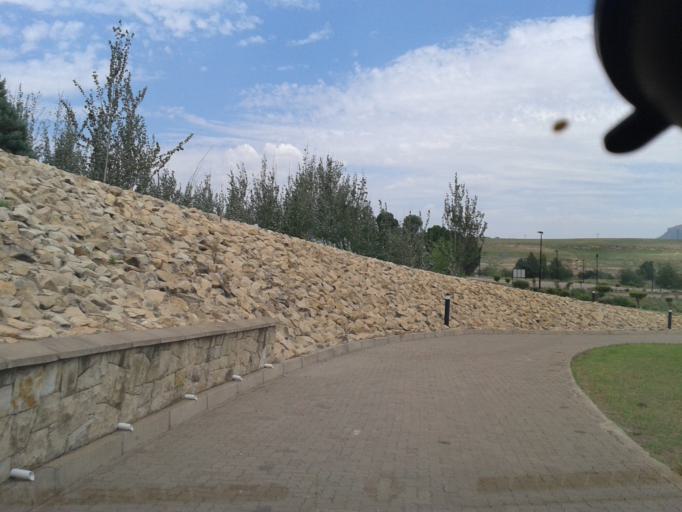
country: LS
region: Maseru
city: Maseru
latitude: -29.3464
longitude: 27.6633
